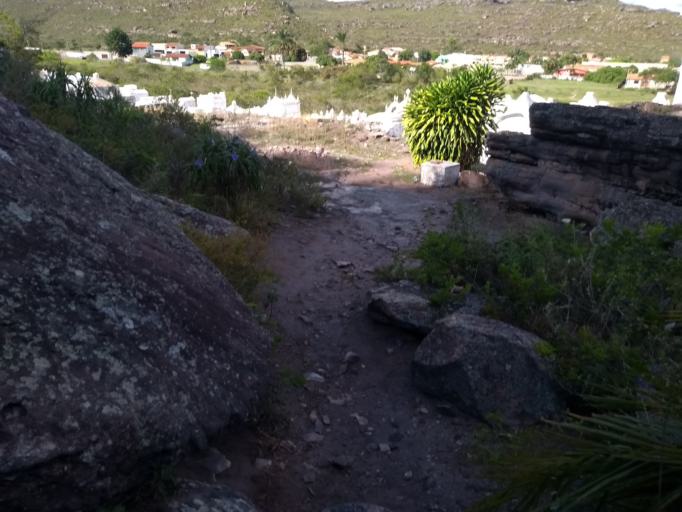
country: BR
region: Bahia
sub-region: Andarai
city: Vera Cruz
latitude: -13.0076
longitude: -41.3773
